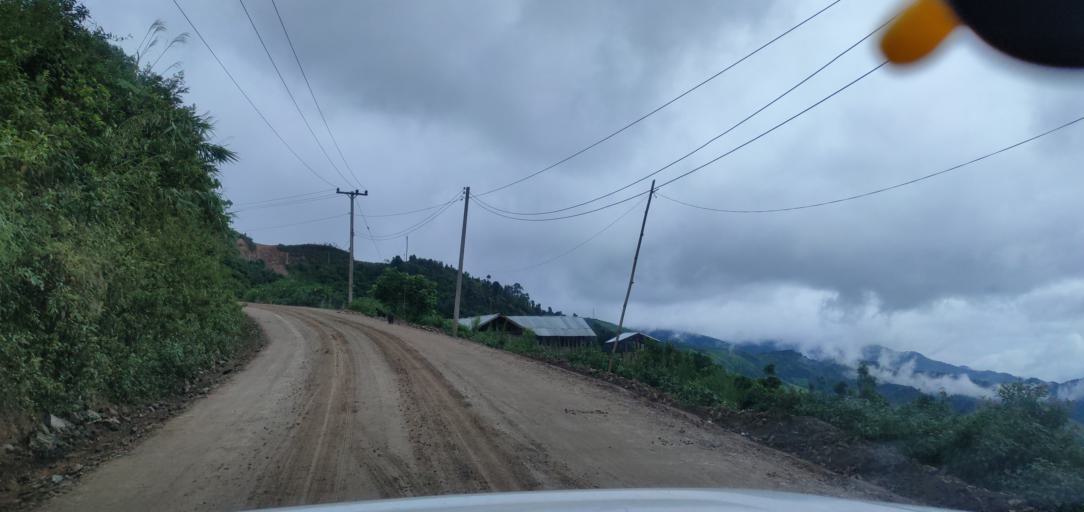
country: LA
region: Phongsali
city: Phongsali
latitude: 21.4282
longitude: 102.1675
